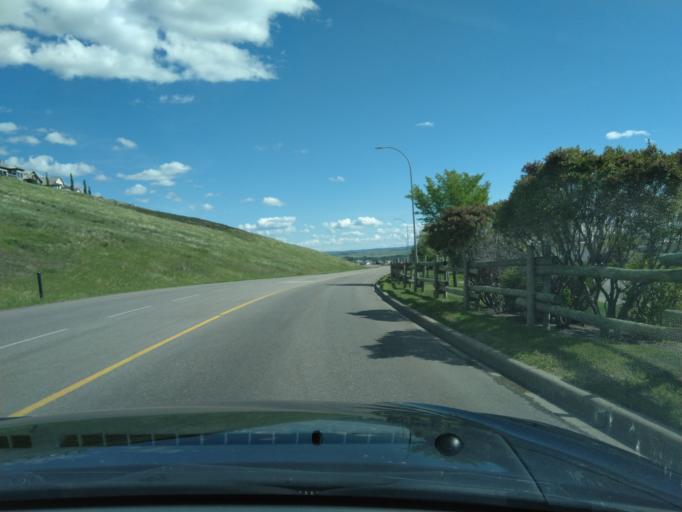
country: CA
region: Alberta
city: Cochrane
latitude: 51.1920
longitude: -114.4311
